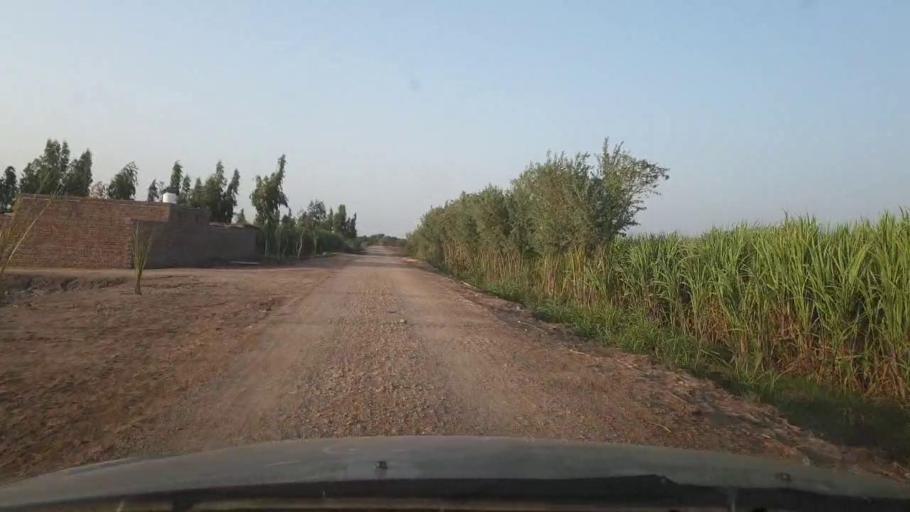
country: PK
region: Sindh
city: Tando Ghulam Ali
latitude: 25.1645
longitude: 68.9748
